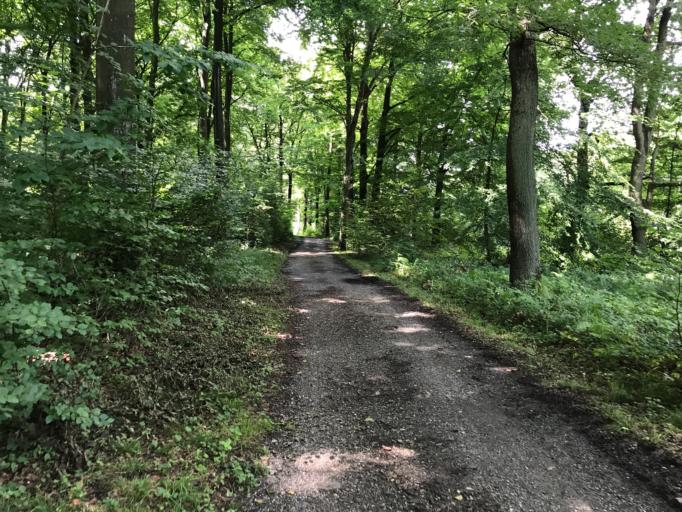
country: DE
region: North Rhine-Westphalia
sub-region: Regierungsbezirk Dusseldorf
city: Duisburg
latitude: 51.4160
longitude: 6.8109
